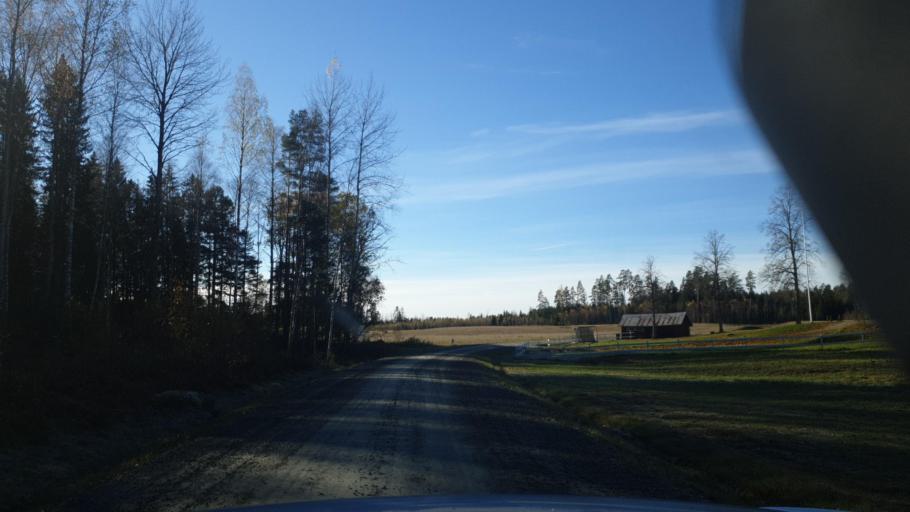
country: SE
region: Vaermland
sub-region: Karlstads Kommun
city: Edsvalla
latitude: 59.4484
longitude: 13.1221
